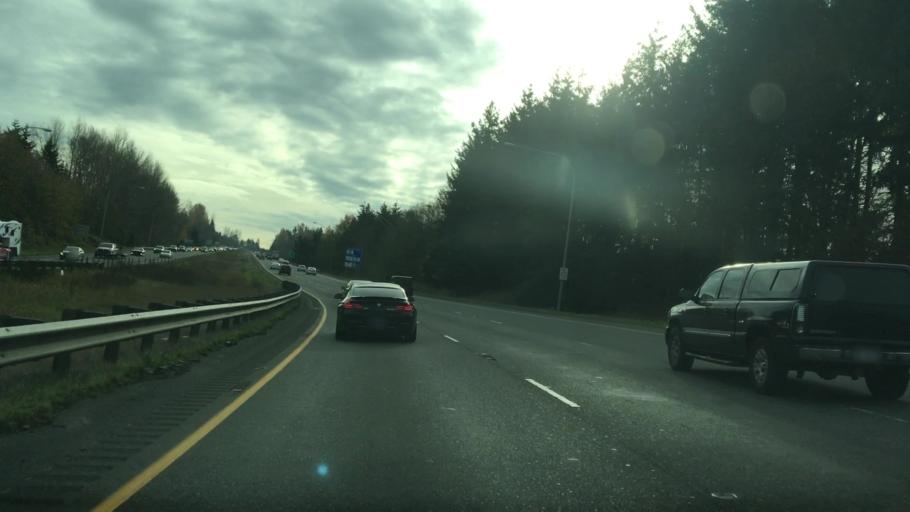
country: US
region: Washington
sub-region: Pierce County
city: Puyallup
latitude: 47.1770
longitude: -122.2970
